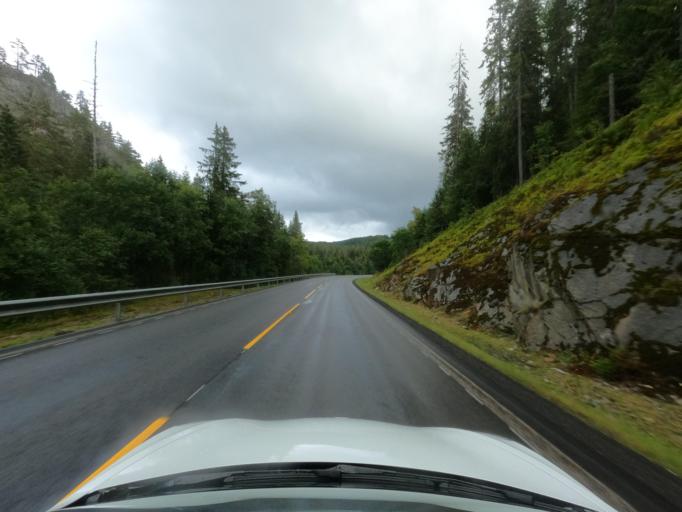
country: NO
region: Telemark
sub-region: Kviteseid
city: Kviteseid
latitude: 59.4438
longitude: 8.5133
